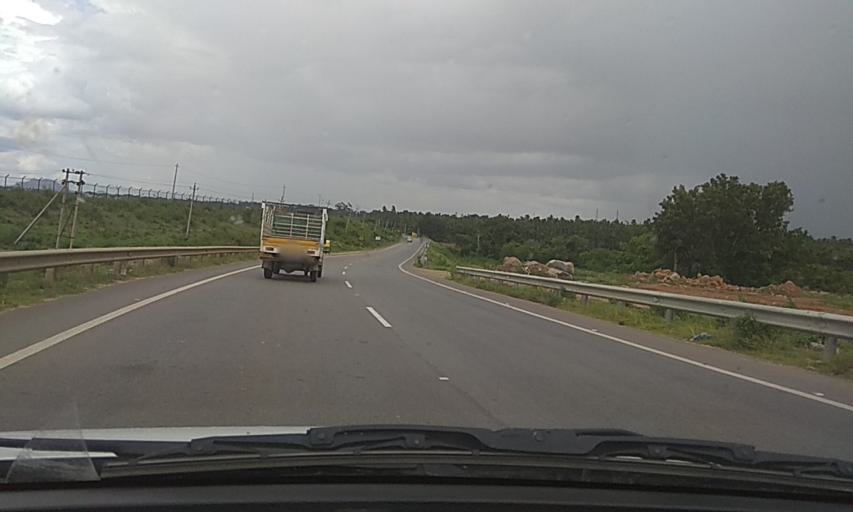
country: IN
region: Karnataka
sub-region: Tumkur
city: Kunigal
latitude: 13.0409
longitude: 77.0218
